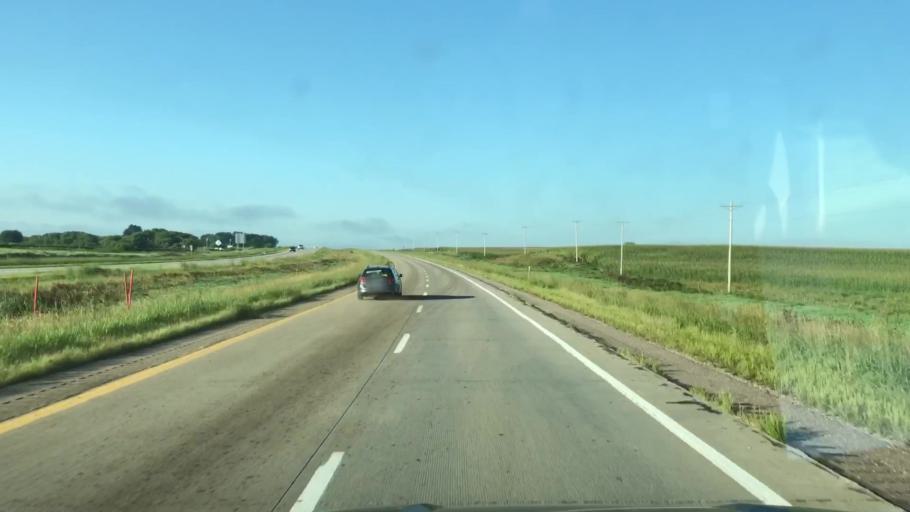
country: US
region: Iowa
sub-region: Sioux County
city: Alton
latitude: 42.9527
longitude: -96.0348
